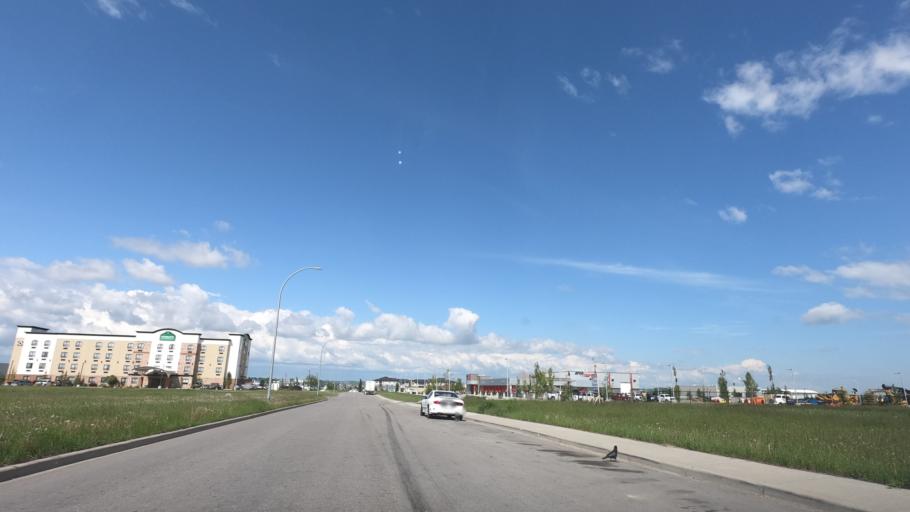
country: CA
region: Alberta
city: Airdrie
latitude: 51.3040
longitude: -114.0058
